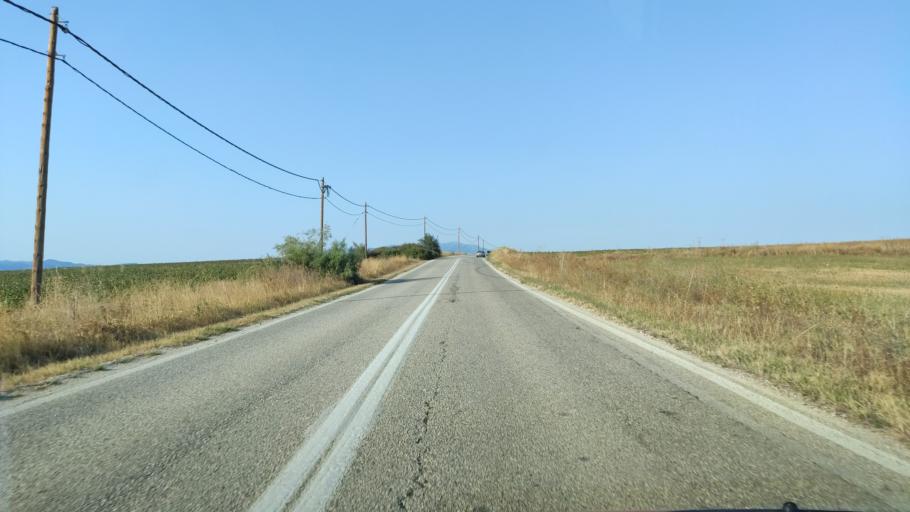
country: GR
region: East Macedonia and Thrace
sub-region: Nomos Rodopis
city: Iasmos
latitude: 40.9876
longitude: 25.1608
